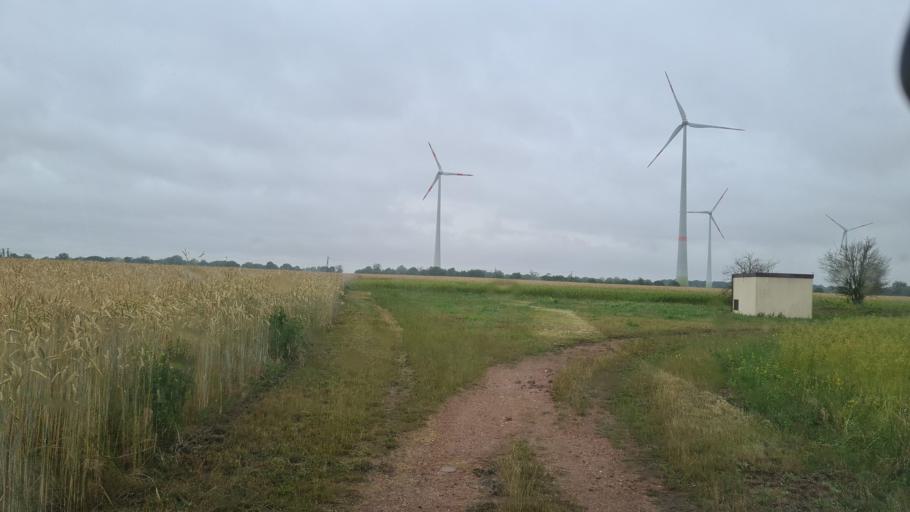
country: DE
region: Brandenburg
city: Juterbog
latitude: 51.9461
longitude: 13.1846
